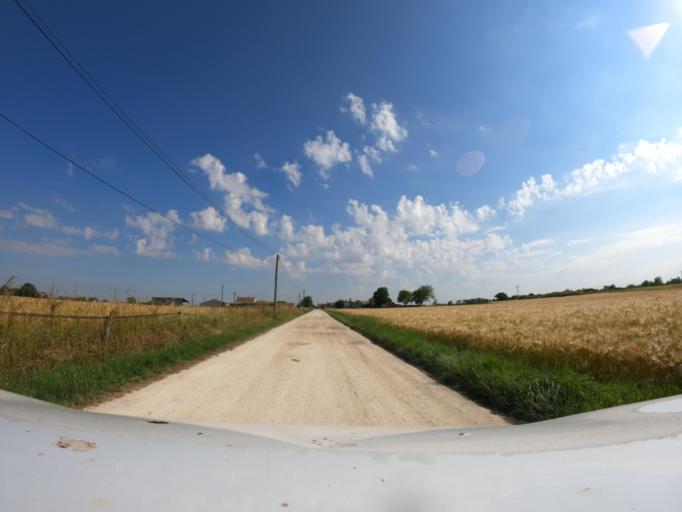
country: FR
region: Pays de la Loire
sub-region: Departement de la Vendee
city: Champagne-les-Marais
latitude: 46.3782
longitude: -1.1000
